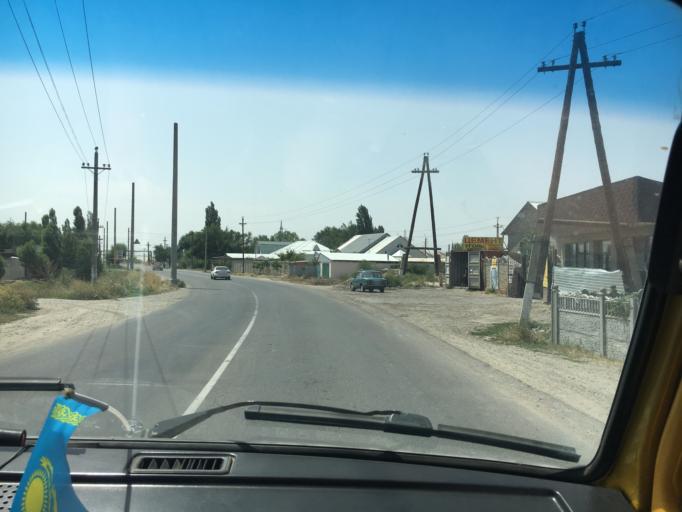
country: KZ
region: Zhambyl
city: Taraz
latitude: 42.8594
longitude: 71.3546
